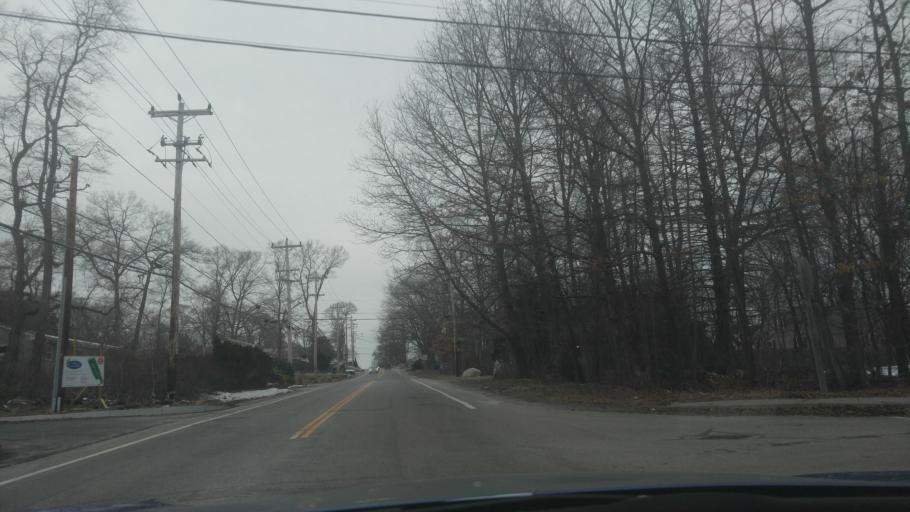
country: US
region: Rhode Island
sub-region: Kent County
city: West Warwick
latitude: 41.6809
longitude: -71.5412
